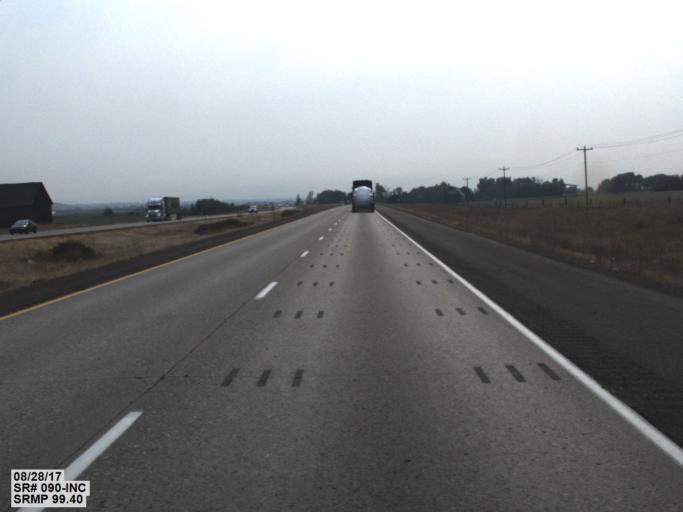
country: US
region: Washington
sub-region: Kittitas County
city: Ellensburg
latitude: 47.0654
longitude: -120.6976
